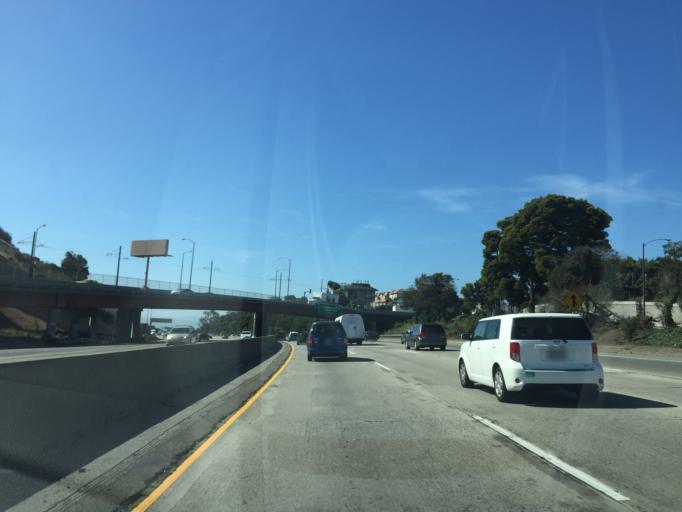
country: US
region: California
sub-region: San Mateo County
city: Brisbane
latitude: 37.7172
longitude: -122.3992
